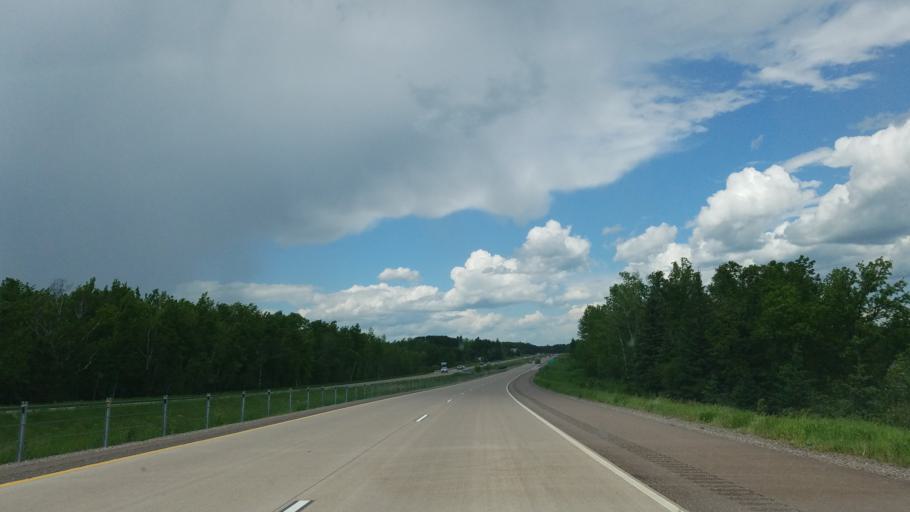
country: US
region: Minnesota
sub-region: Carlton County
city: Moose Lake
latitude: 46.4747
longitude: -92.7150
